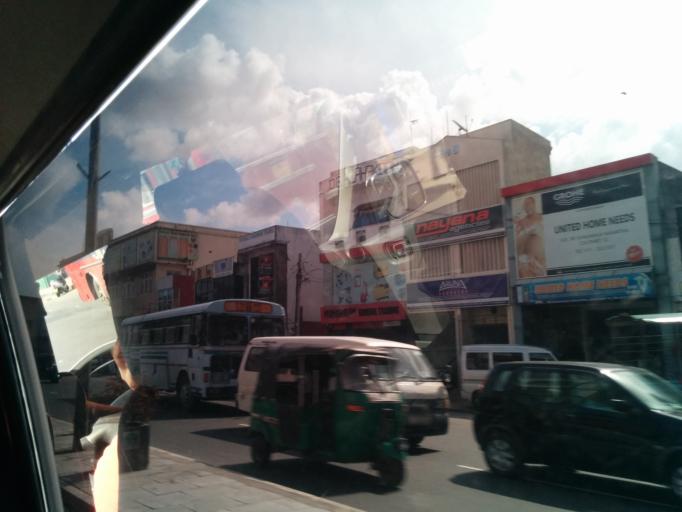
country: LK
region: Western
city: Colombo
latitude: 6.9398
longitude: 79.8659
